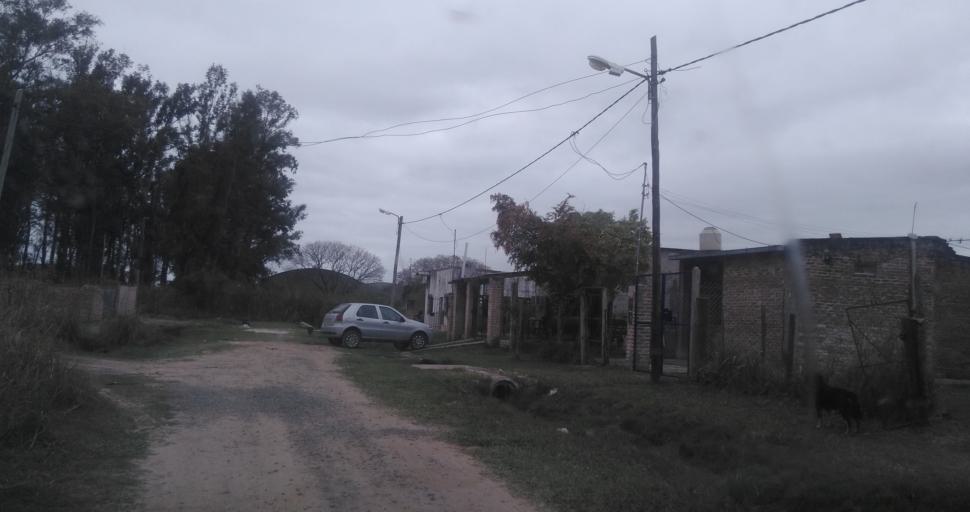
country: AR
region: Chaco
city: Fontana
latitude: -27.4460
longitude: -59.0295
